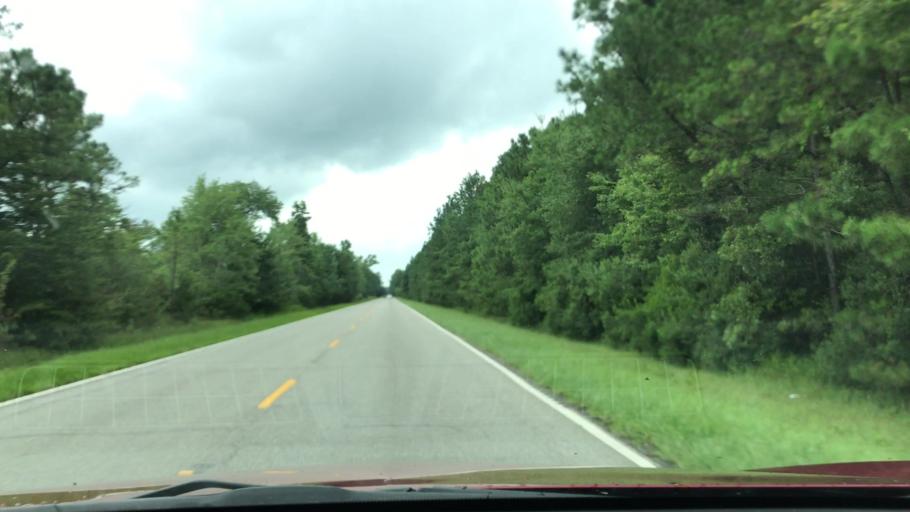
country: US
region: South Carolina
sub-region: Georgetown County
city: Georgetown
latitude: 33.5381
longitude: -79.2316
